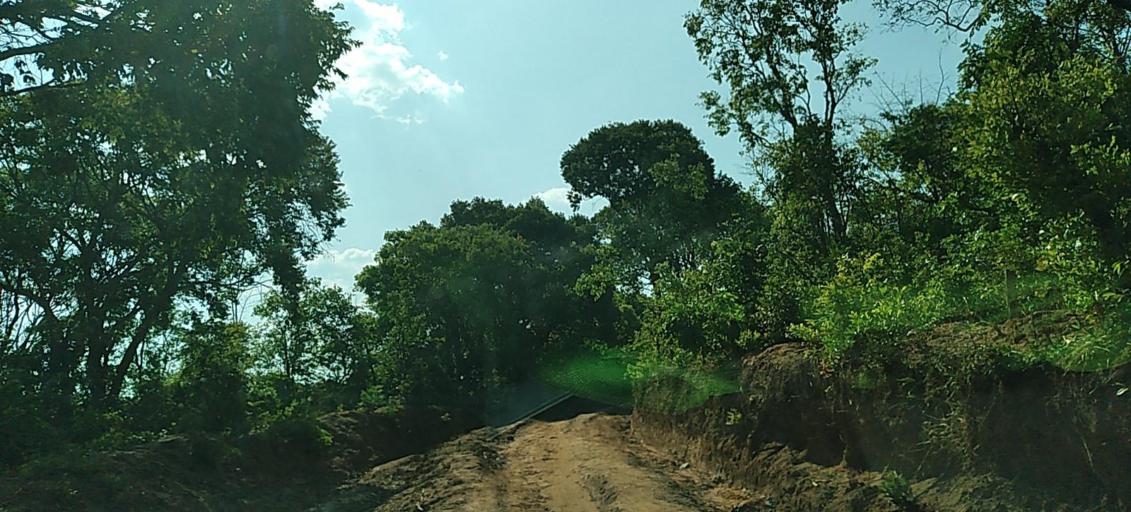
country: ZM
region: North-Western
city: Mwinilunga
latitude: -11.3004
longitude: 24.8710
